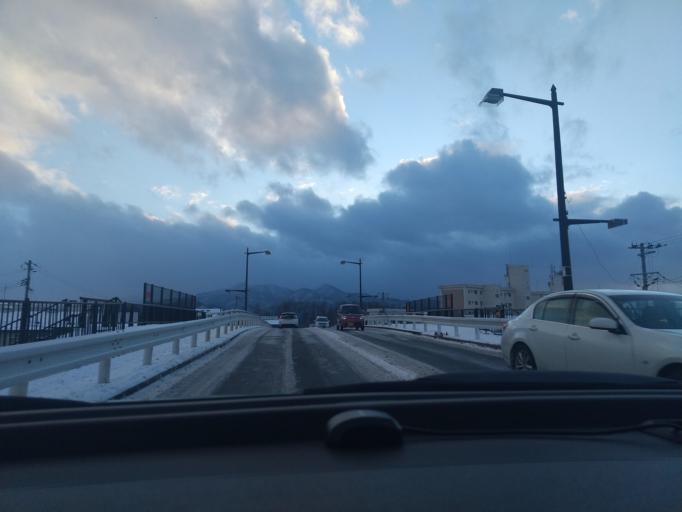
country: JP
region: Iwate
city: Morioka-shi
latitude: 39.7103
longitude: 141.1175
